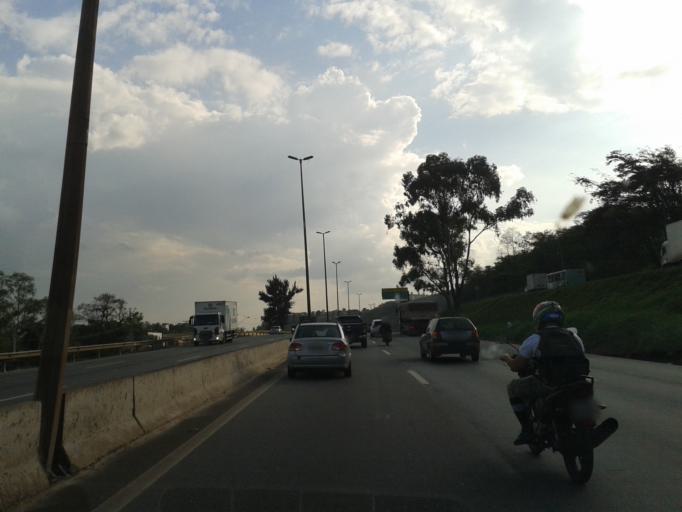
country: BR
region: Minas Gerais
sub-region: Belo Horizonte
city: Belo Horizonte
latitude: -19.8898
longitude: -43.9727
